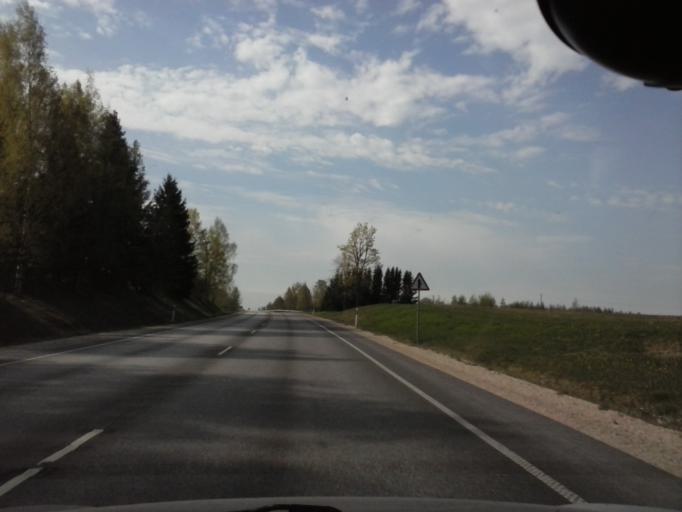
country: EE
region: Tartu
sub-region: UElenurme vald
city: Ulenurme
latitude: 58.1885
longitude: 26.6941
